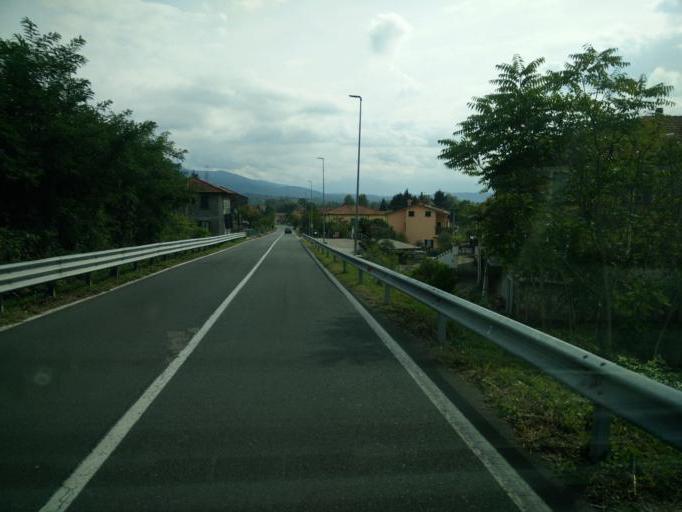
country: IT
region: Tuscany
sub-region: Provincia di Massa-Carrara
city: Filattiera
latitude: 44.3389
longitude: 9.9131
